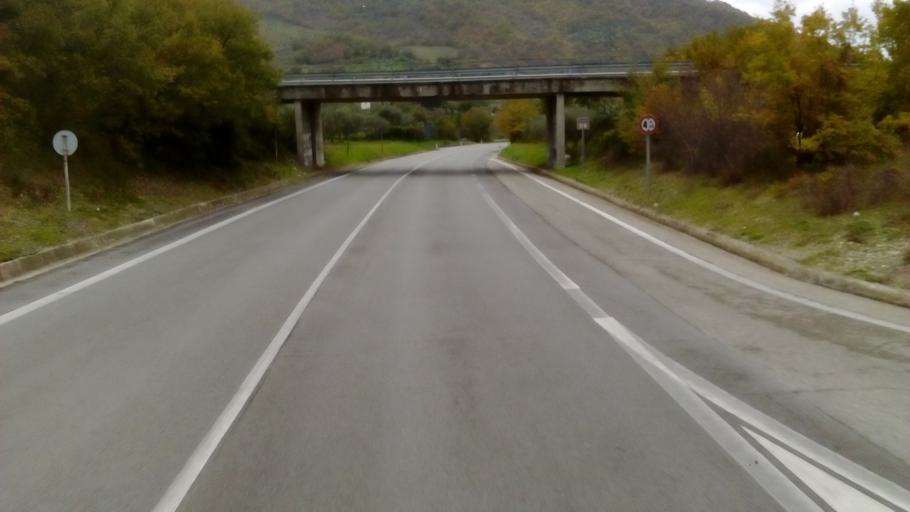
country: IT
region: Molise
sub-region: Provincia di Campobasso
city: Roccavivara
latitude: 41.8557
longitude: 14.6043
